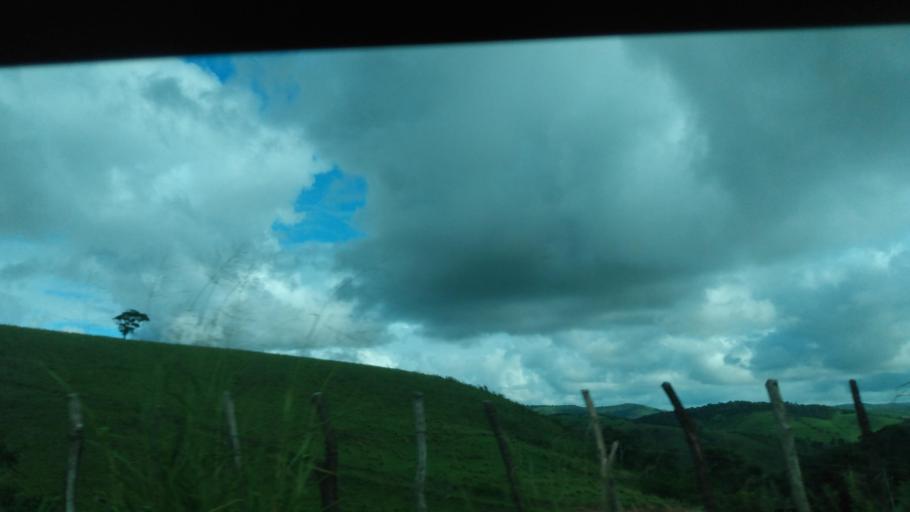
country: BR
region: Pernambuco
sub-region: Maraial
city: Maraial
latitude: -8.7873
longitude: -35.9047
